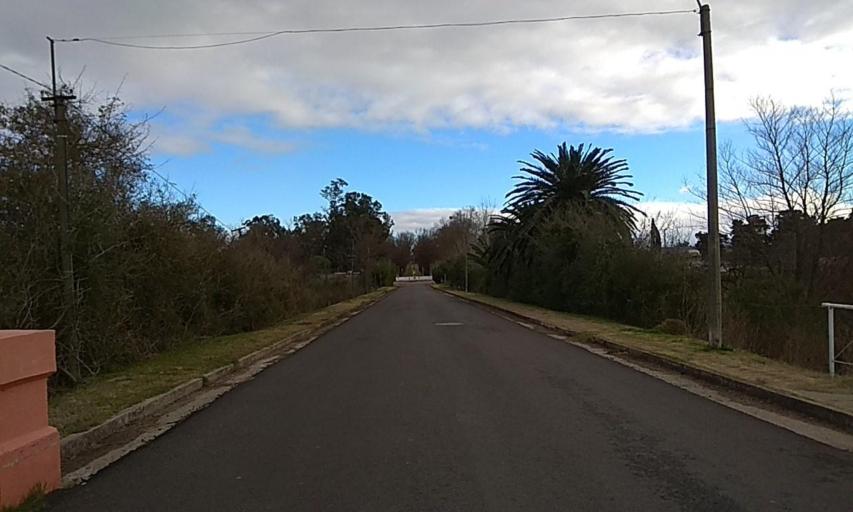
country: UY
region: Florida
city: Florida
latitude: -34.1036
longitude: -56.2228
